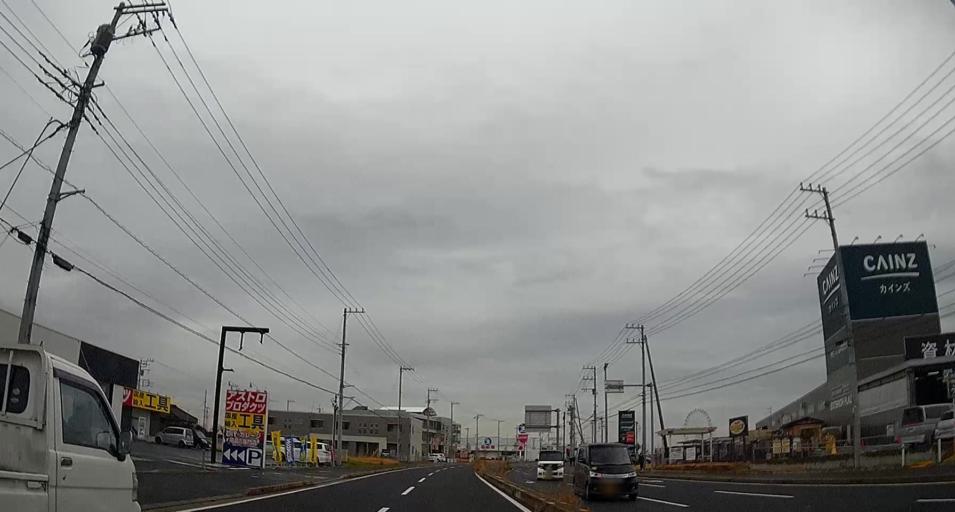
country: JP
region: Chiba
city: Kisarazu
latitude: 35.4321
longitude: 139.9329
